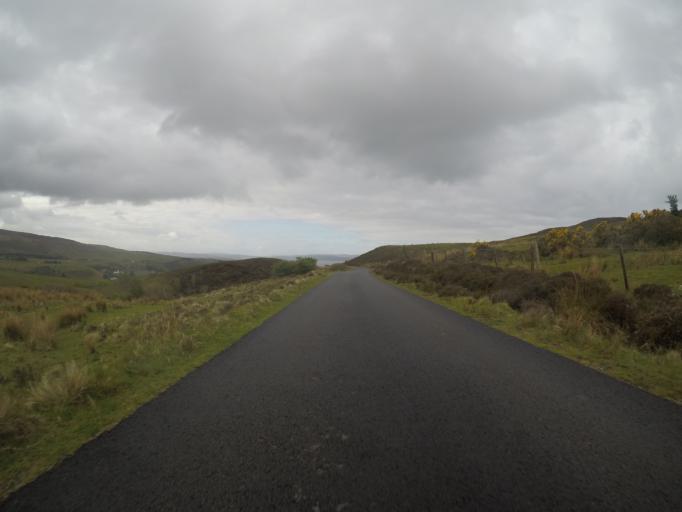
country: GB
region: Scotland
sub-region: Highland
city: Portree
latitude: 57.5972
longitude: -6.3572
